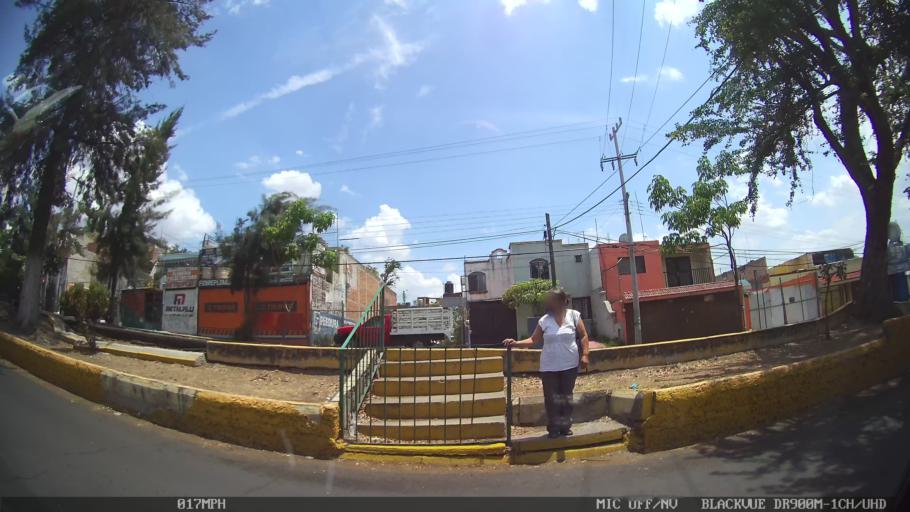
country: MX
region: Jalisco
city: Tonala
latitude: 20.6300
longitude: -103.2639
